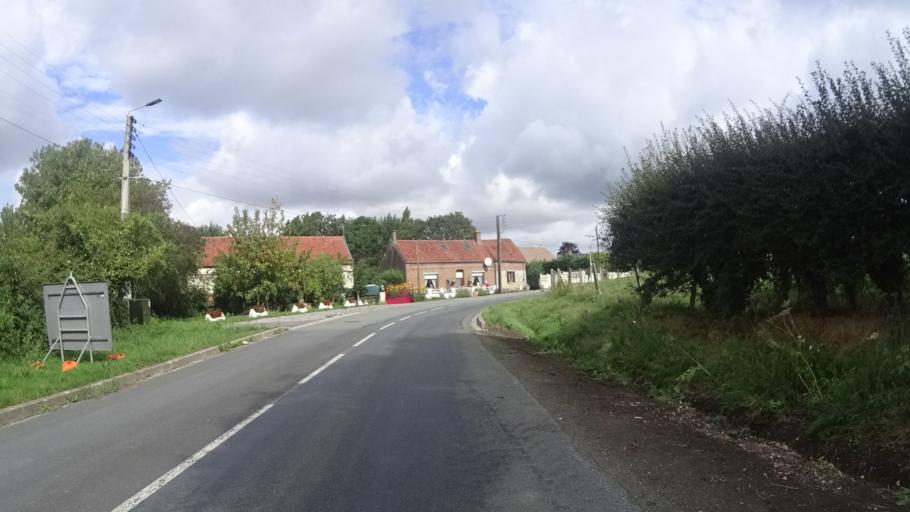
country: FR
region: Nord-Pas-de-Calais
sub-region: Departement du Nord
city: Bousies
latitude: 50.0962
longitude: 3.6390
